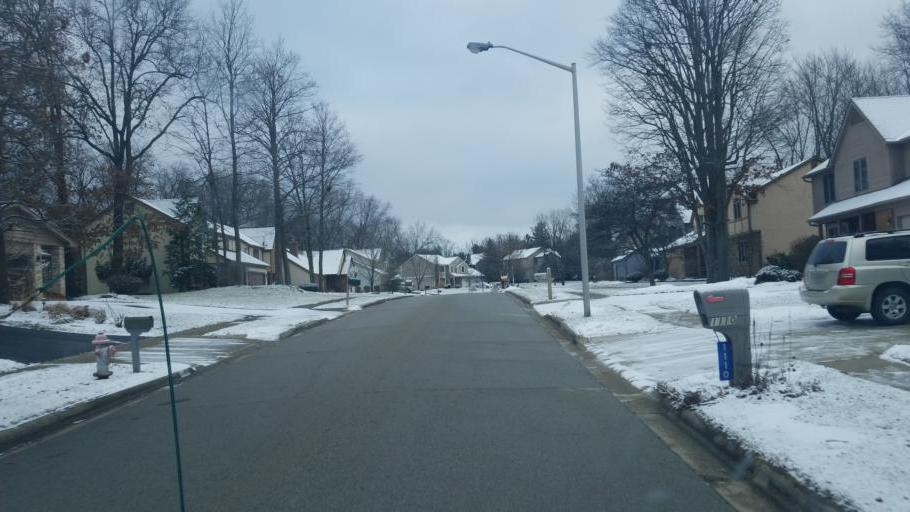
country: US
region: Ohio
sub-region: Franklin County
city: Gahanna
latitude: 40.0469
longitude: -82.8528
